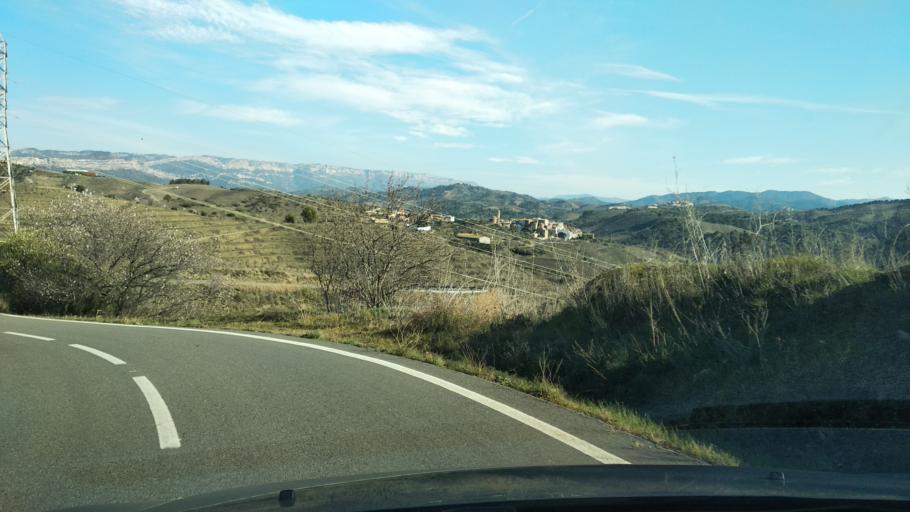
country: ES
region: Catalonia
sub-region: Provincia de Tarragona
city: el Masroig
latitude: 41.1789
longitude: 0.7403
